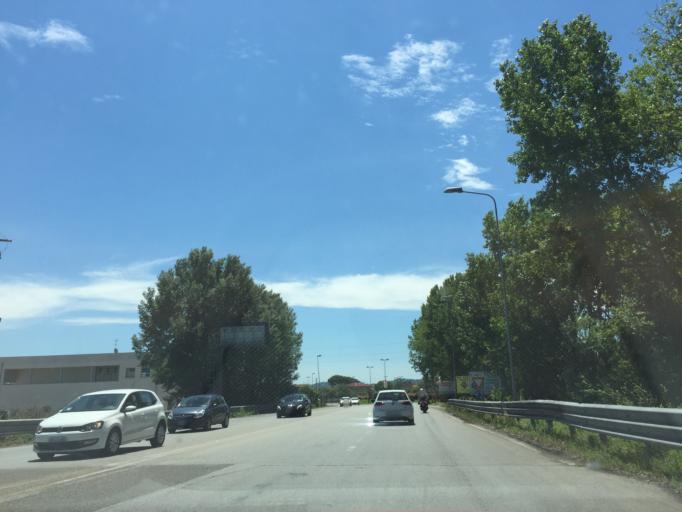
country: IT
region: Tuscany
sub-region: Province of Pisa
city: San Miniato
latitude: 43.6927
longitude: 10.7900
